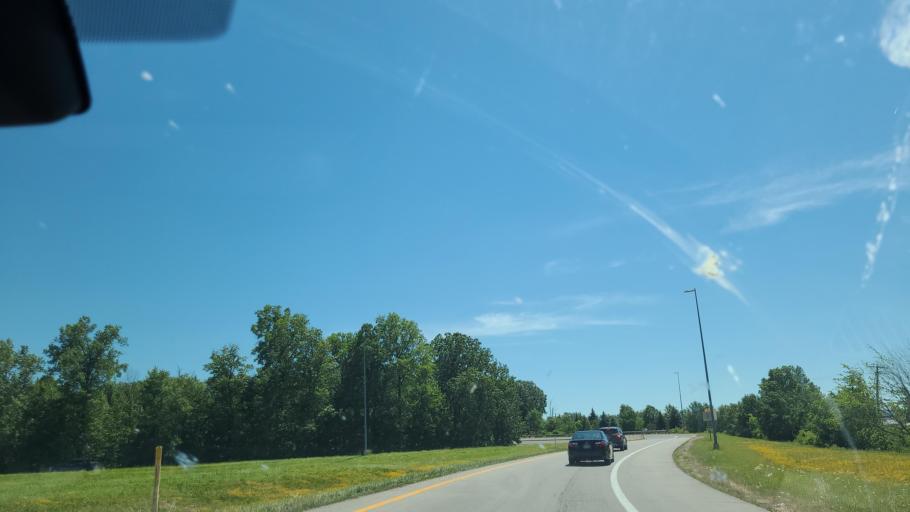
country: US
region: Ohio
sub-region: Lorain County
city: Elyria
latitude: 41.3932
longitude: -82.1172
